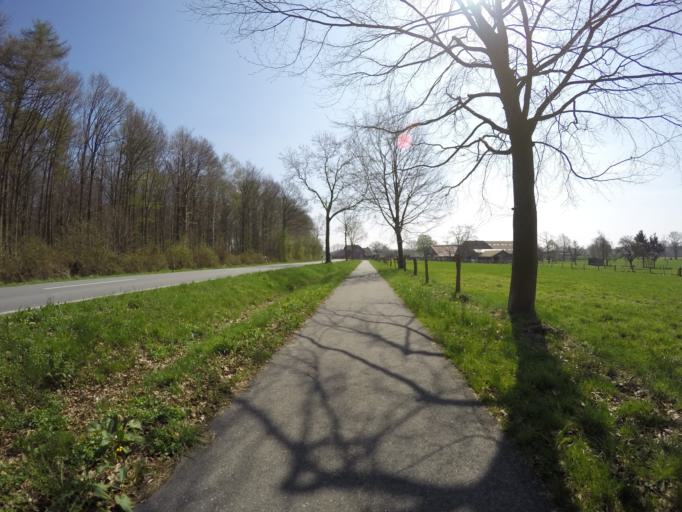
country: DE
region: Schleswig-Holstein
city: Bilsen
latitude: 53.7493
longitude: 9.8790
